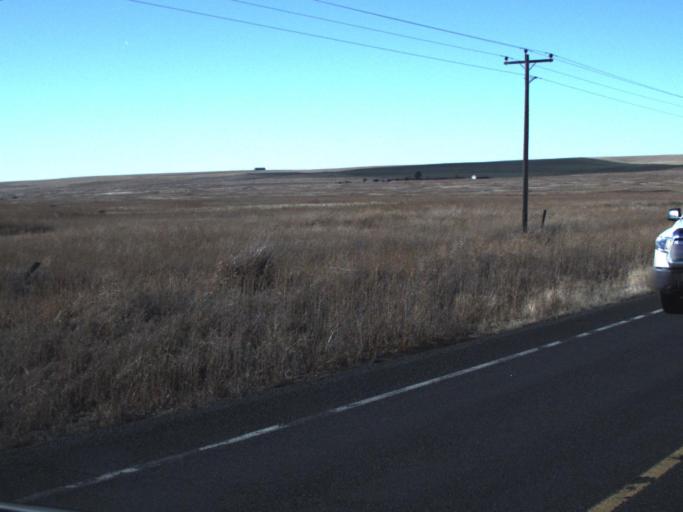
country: US
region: Washington
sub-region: Adams County
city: Ritzville
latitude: 47.0427
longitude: -118.3490
